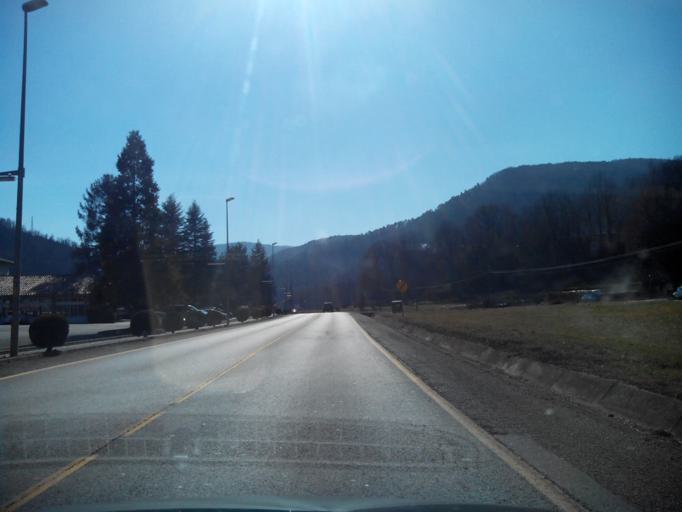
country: ES
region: Catalonia
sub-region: Provincia de Girona
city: Ripoll
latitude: 42.1832
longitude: 2.1956
